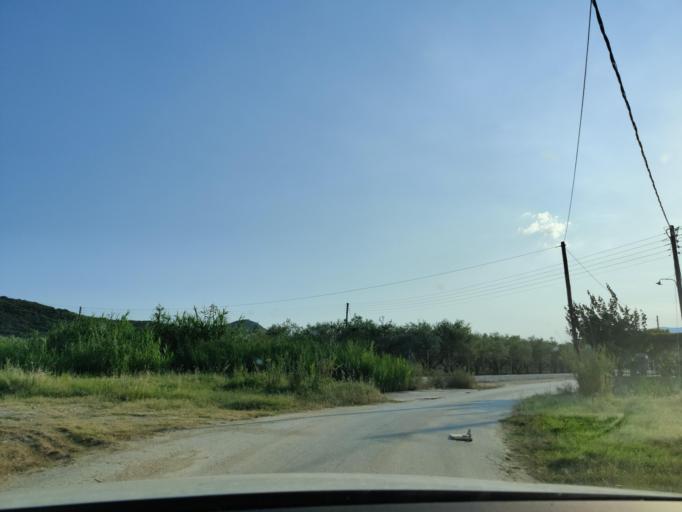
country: GR
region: East Macedonia and Thrace
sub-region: Nomos Kavalas
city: Nea Peramos
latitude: 40.8299
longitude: 24.3032
